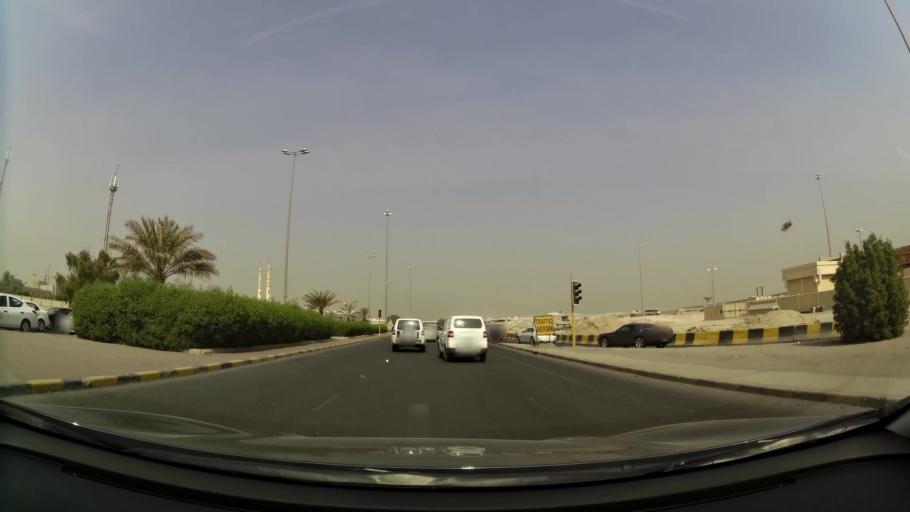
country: KW
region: Al Asimah
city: Ar Rabiyah
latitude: 29.2684
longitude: 47.9079
